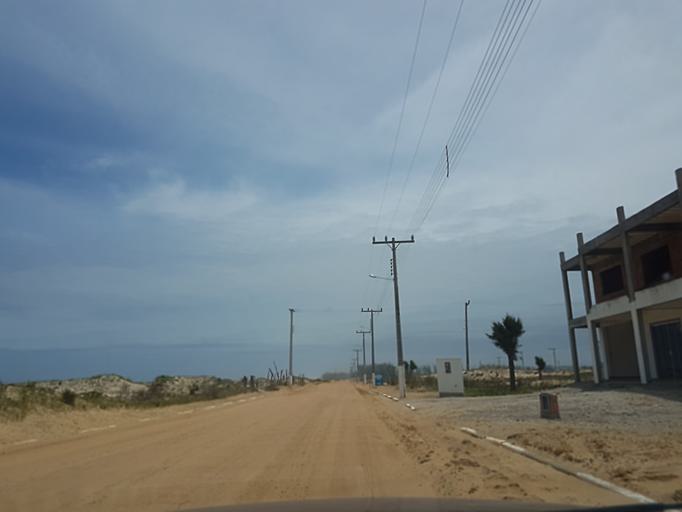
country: BR
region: Santa Catarina
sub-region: Jaguaruna
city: Jaguaruna
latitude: -28.6654
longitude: -48.9648
